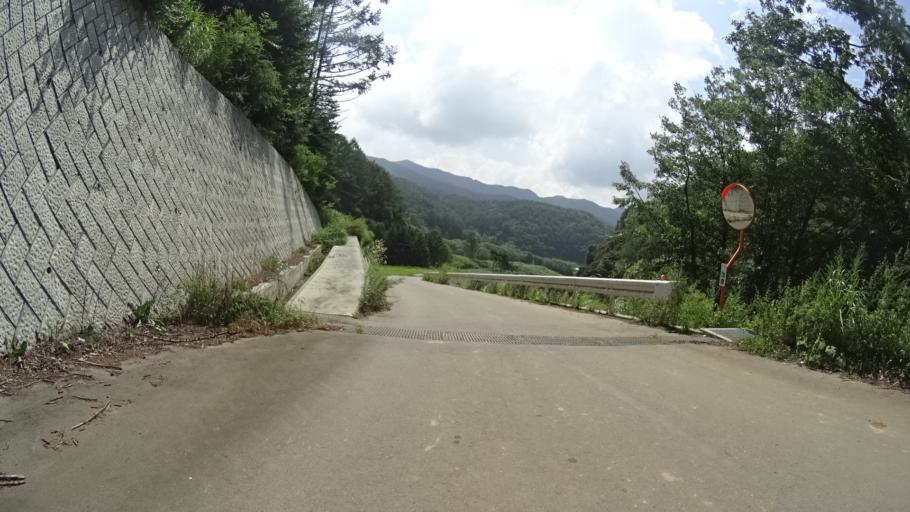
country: JP
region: Yamanashi
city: Nirasaki
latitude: 35.9051
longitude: 138.4688
